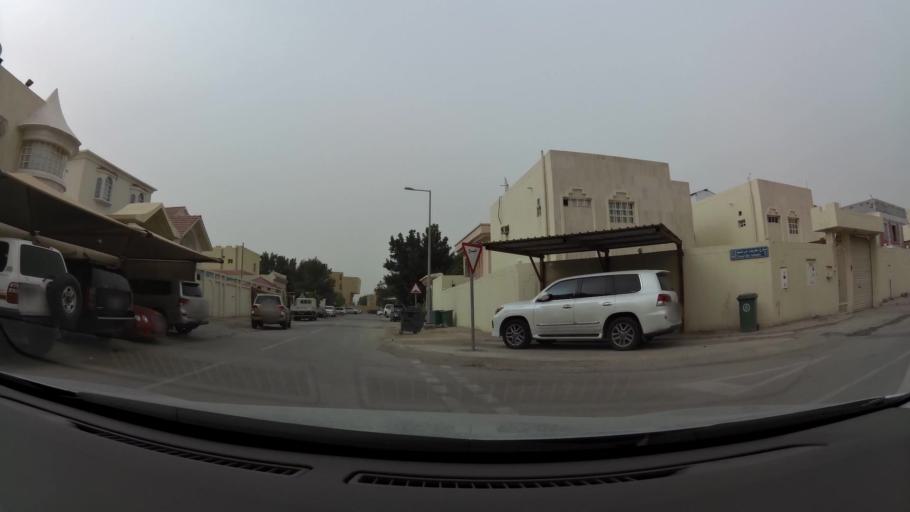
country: QA
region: Baladiyat ad Dawhah
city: Doha
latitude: 25.2539
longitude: 51.4948
